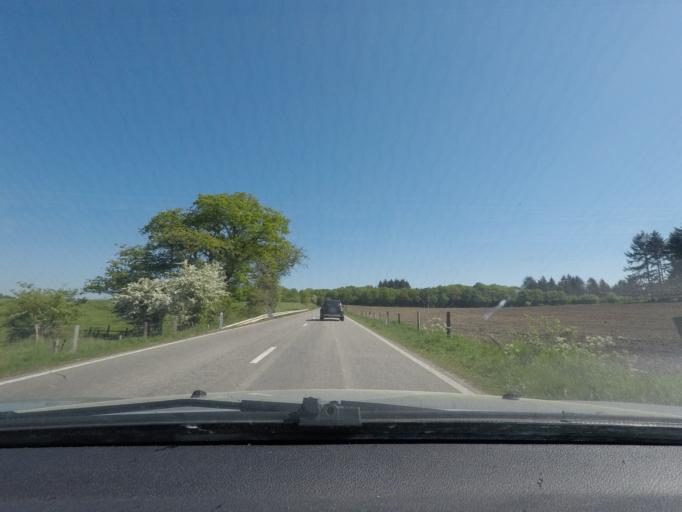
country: BE
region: Wallonia
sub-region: Province de Namur
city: Rochefort
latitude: 50.2067
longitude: 5.1441
